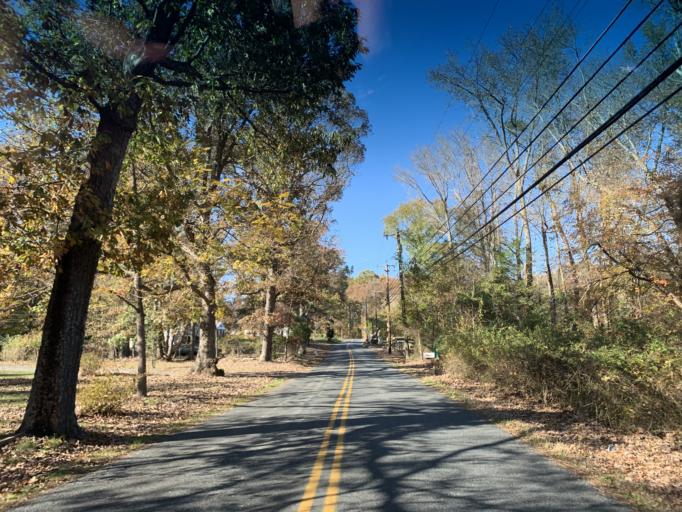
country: US
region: Maryland
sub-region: Harford County
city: Joppatowne
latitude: 39.4489
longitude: -76.3367
